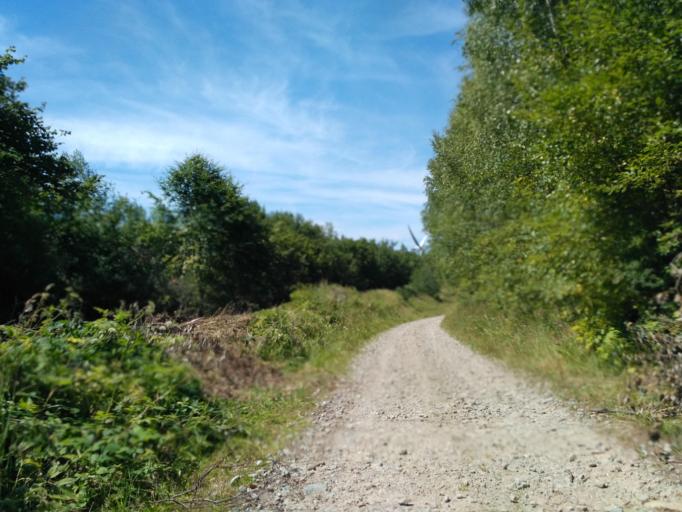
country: PL
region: Subcarpathian Voivodeship
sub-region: Powiat sanocki
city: Bukowsko
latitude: 49.4865
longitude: 22.0922
